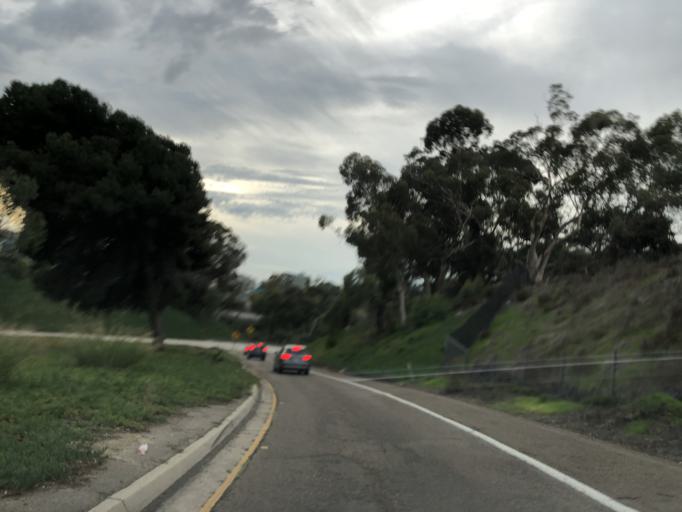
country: US
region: California
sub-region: San Diego County
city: San Diego
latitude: 32.7251
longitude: -117.1528
